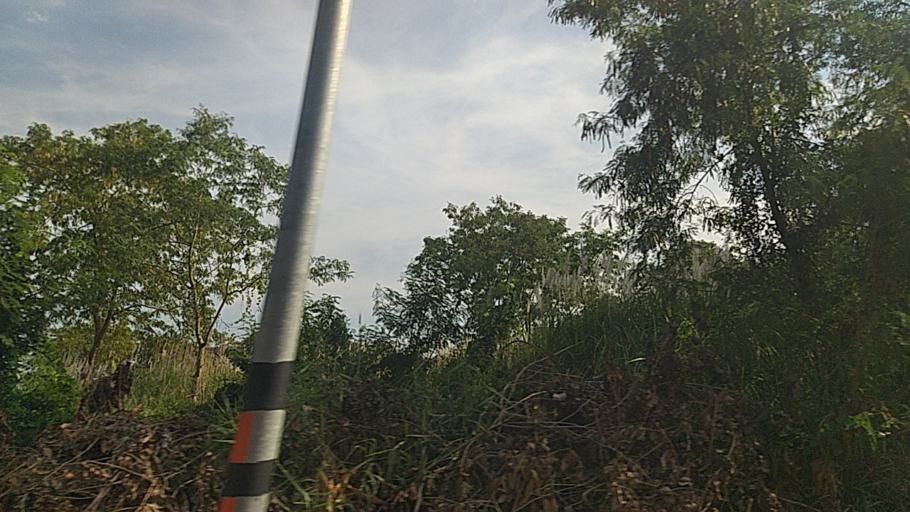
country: TH
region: Pathum Thani
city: Thanyaburi
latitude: 14.0195
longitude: 100.7370
